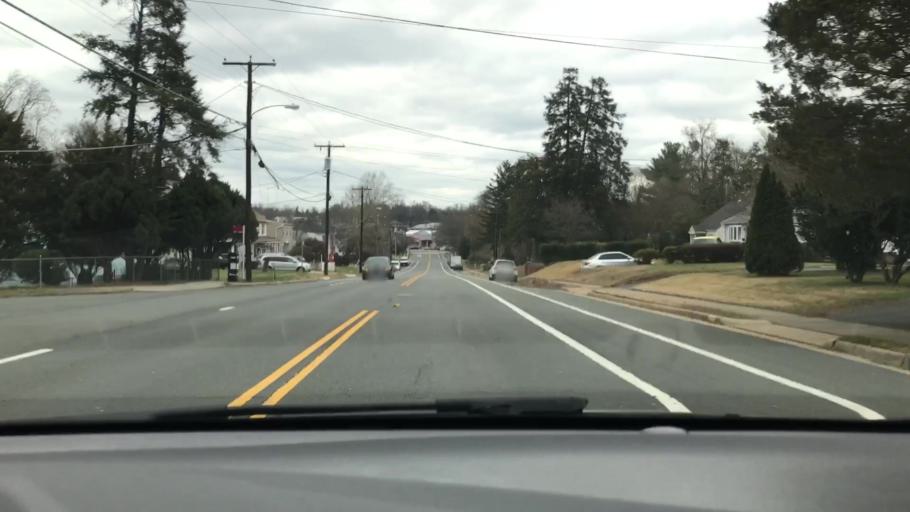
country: US
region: Virginia
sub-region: Fairfax County
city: Jefferson
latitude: 38.8639
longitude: -77.1764
